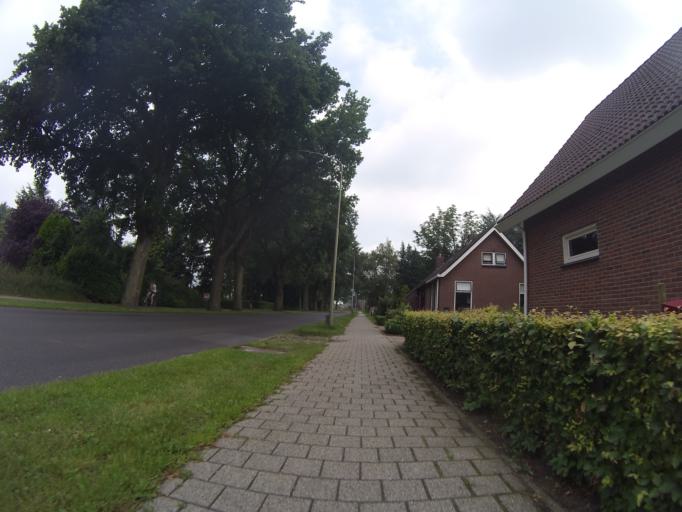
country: NL
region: Drenthe
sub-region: Gemeente Emmen
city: Emmen
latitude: 52.8122
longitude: 6.9083
